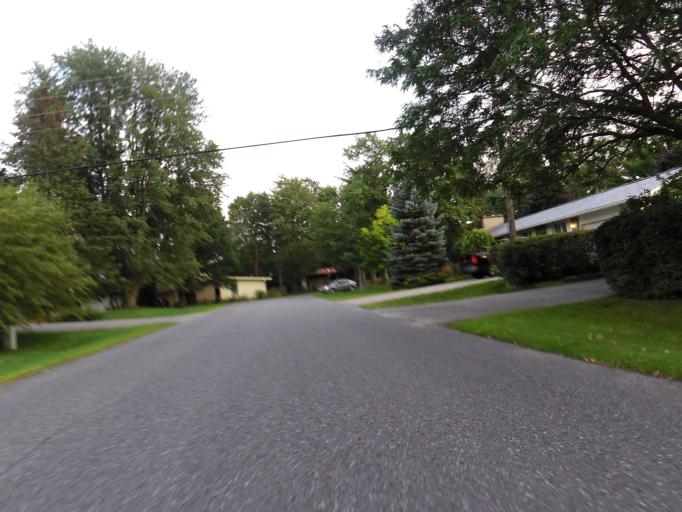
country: CA
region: Ontario
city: Bells Corners
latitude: 45.3236
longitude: -75.8192
